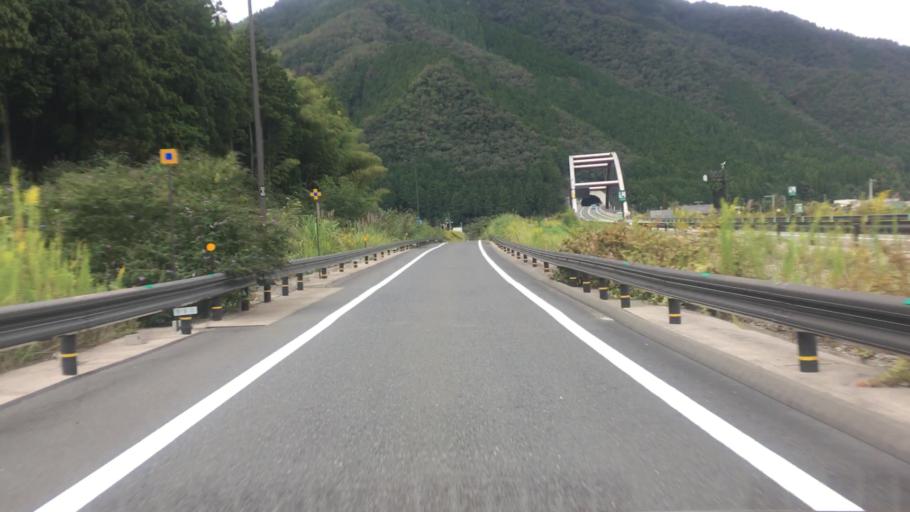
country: JP
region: Hyogo
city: Toyooka
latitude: 35.3588
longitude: 134.7620
